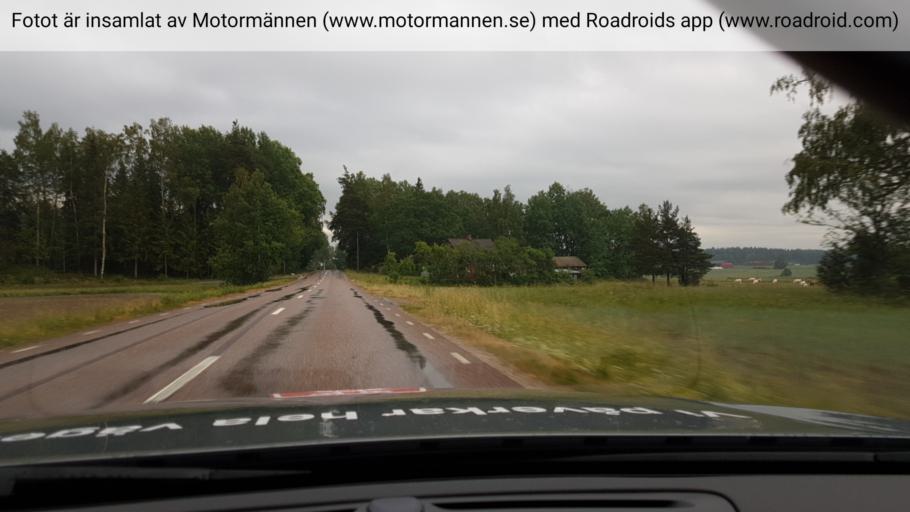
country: SE
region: Vaestmanland
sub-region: Surahammars Kommun
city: Ramnas
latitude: 59.9500
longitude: 16.2528
